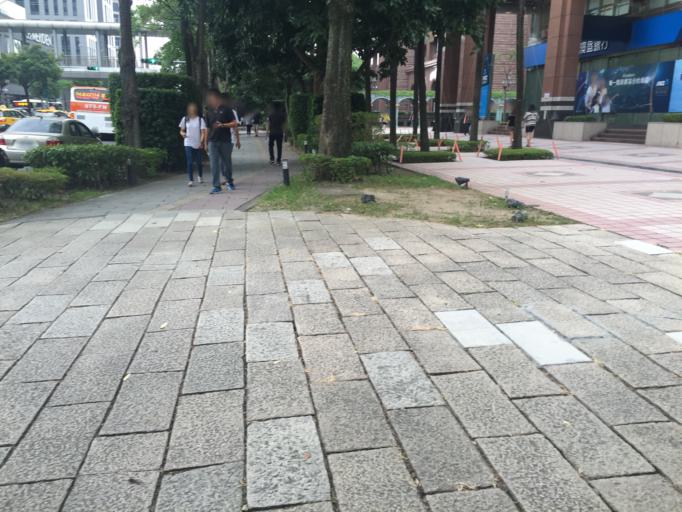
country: TW
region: Taipei
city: Taipei
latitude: 25.0369
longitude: 121.5686
